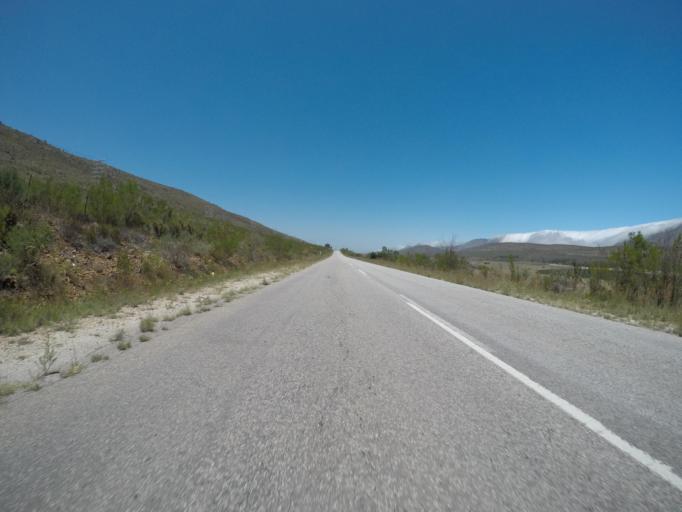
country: ZA
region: Eastern Cape
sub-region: Cacadu District Municipality
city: Kareedouw
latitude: -33.8373
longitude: 23.9208
